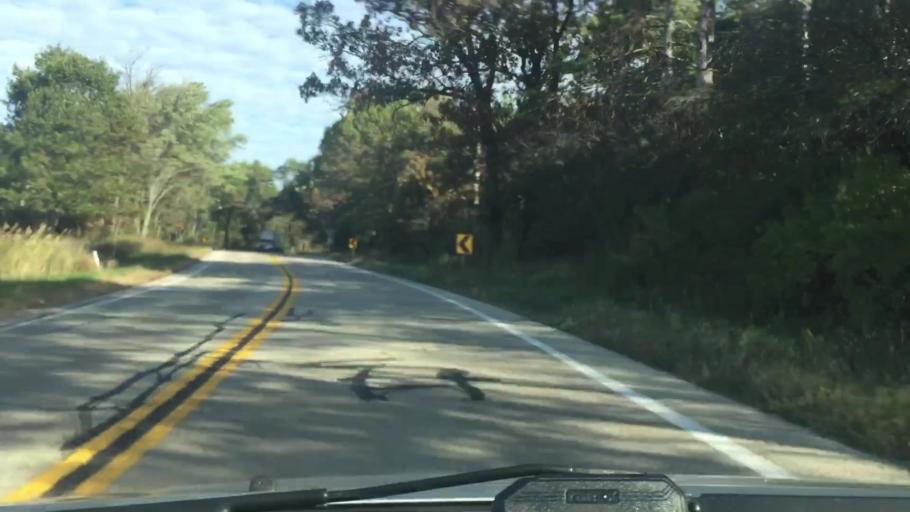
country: US
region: Wisconsin
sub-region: Waukesha County
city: Eagle
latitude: 42.9290
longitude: -88.4659
